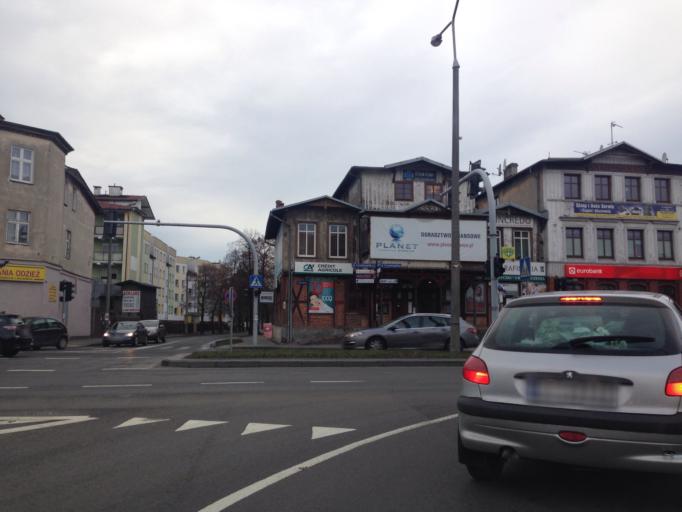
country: PL
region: Kujawsko-Pomorskie
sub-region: Torun
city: Torun
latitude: 53.0240
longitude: 18.6118
